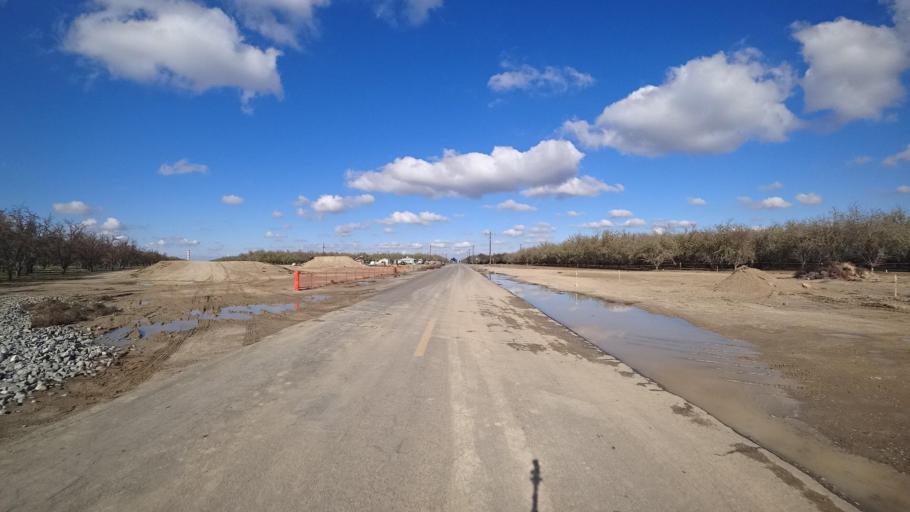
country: US
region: California
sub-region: Kern County
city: Delano
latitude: 35.7234
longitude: -119.3659
